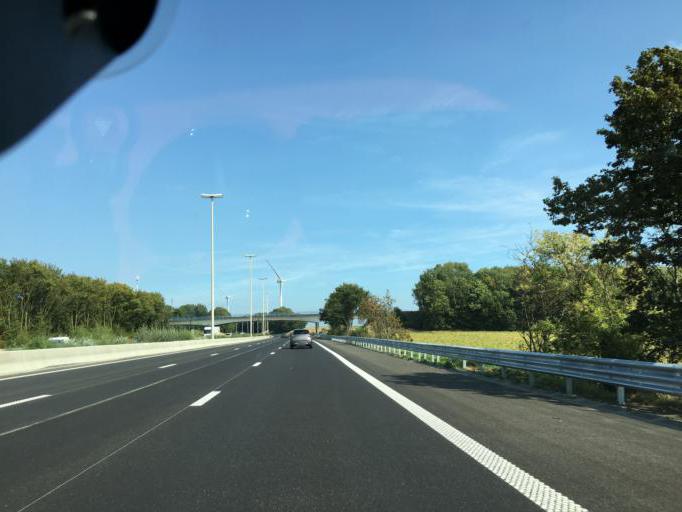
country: BE
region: Wallonia
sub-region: Province de Namur
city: Namur
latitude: 50.5224
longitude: 4.9060
